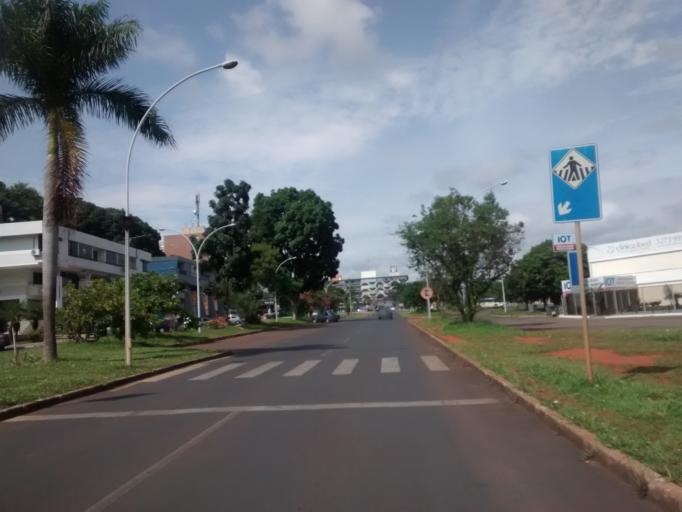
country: BR
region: Federal District
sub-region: Brasilia
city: Brasilia
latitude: -15.7377
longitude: -47.8971
